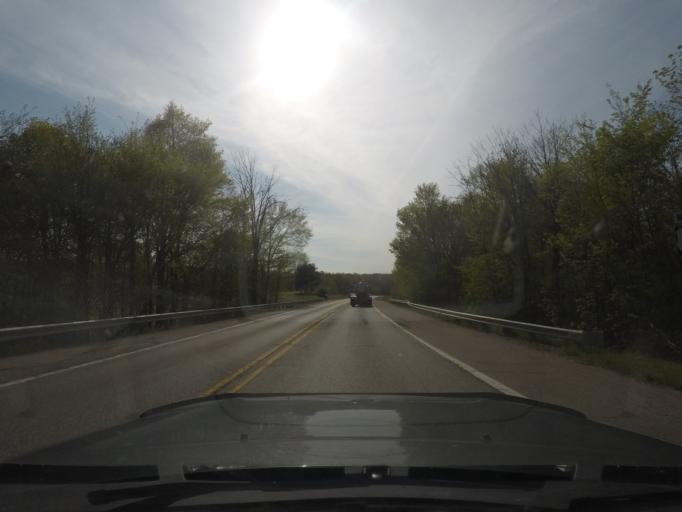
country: US
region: Michigan
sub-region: Berrien County
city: Buchanan
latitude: 41.7933
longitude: -86.4416
